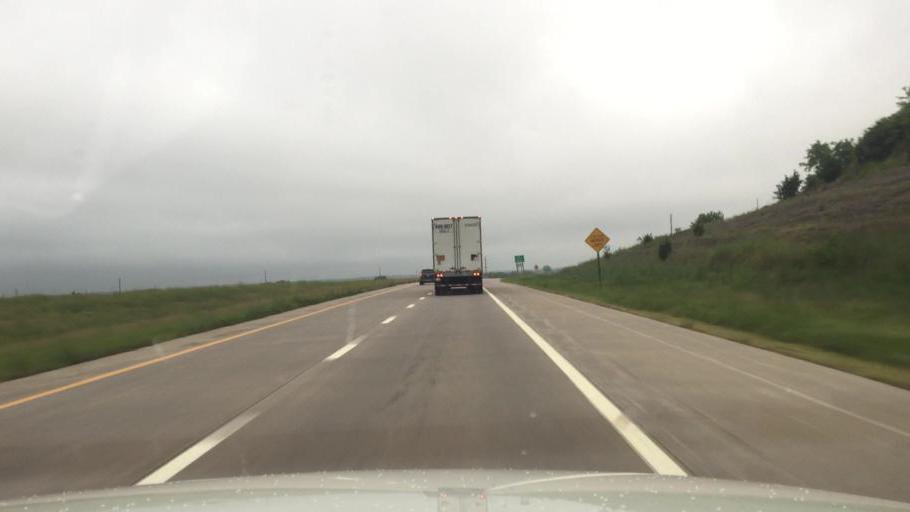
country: US
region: Kansas
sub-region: Montgomery County
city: Cherryvale
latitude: 37.2136
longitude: -95.5852
